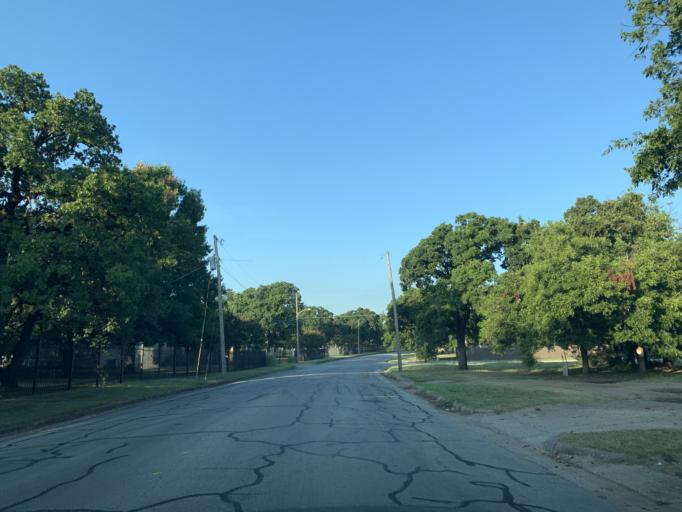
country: US
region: Texas
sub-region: Tarrant County
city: River Oaks
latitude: 32.7708
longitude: -97.3495
